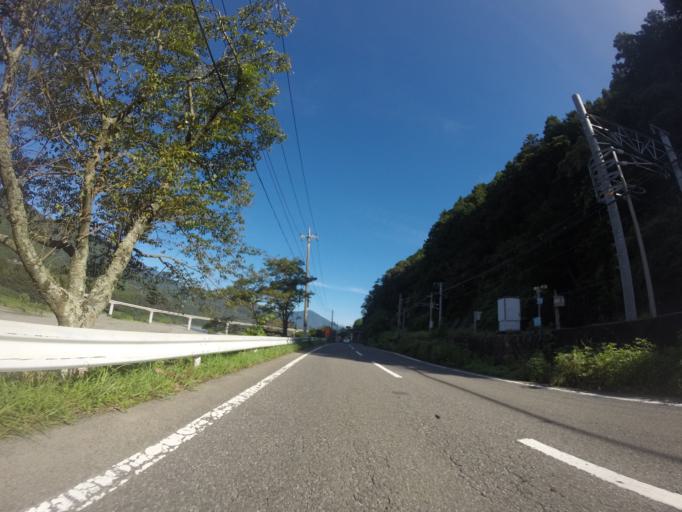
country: JP
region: Shizuoka
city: Fujinomiya
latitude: 35.3055
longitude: 138.4564
